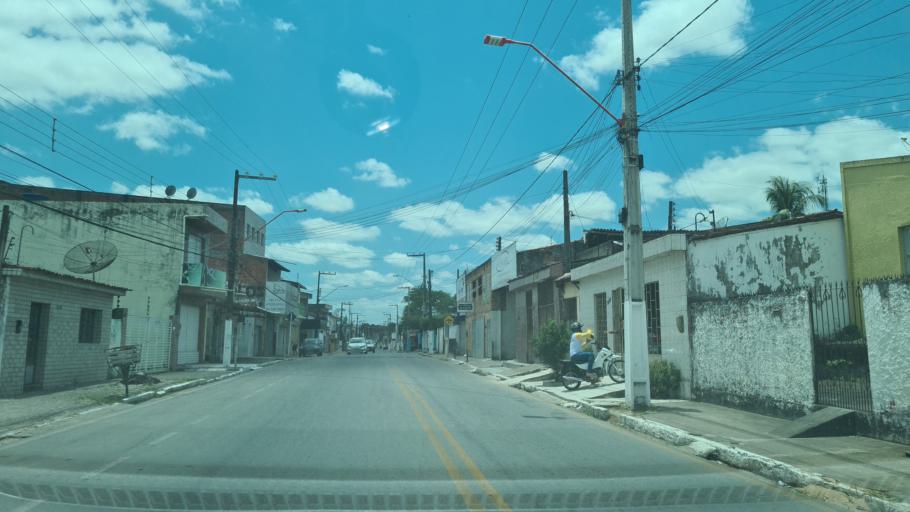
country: BR
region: Alagoas
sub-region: Uniao Dos Palmares
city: Uniao dos Palmares
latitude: -9.1635
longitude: -36.0279
